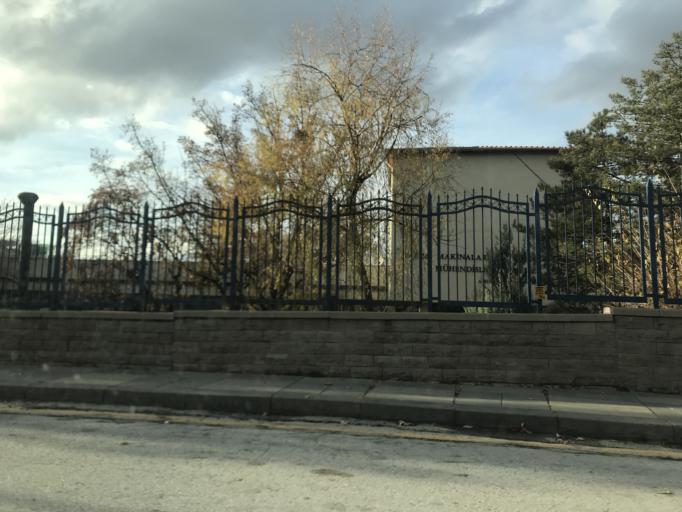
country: TR
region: Ankara
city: Ankara
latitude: 39.9614
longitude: 32.8674
